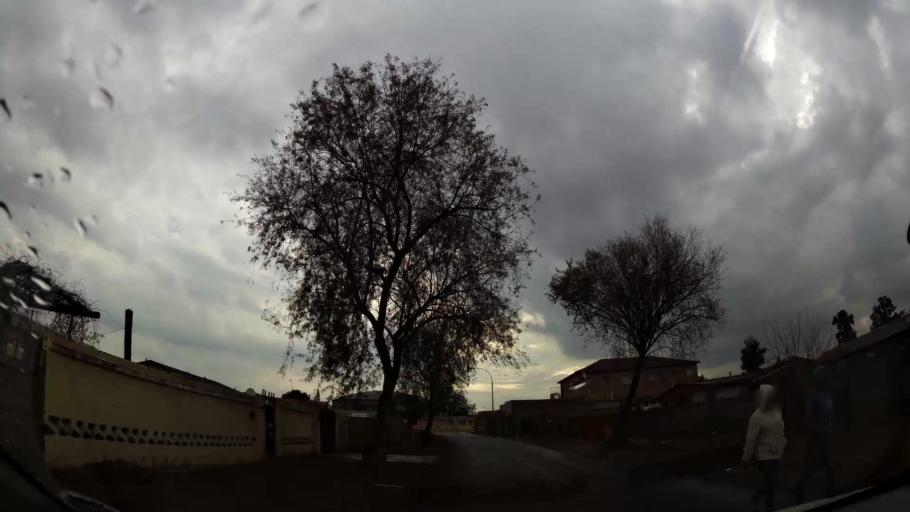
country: ZA
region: Gauteng
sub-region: Ekurhuleni Metropolitan Municipality
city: Germiston
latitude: -26.3778
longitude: 28.1286
